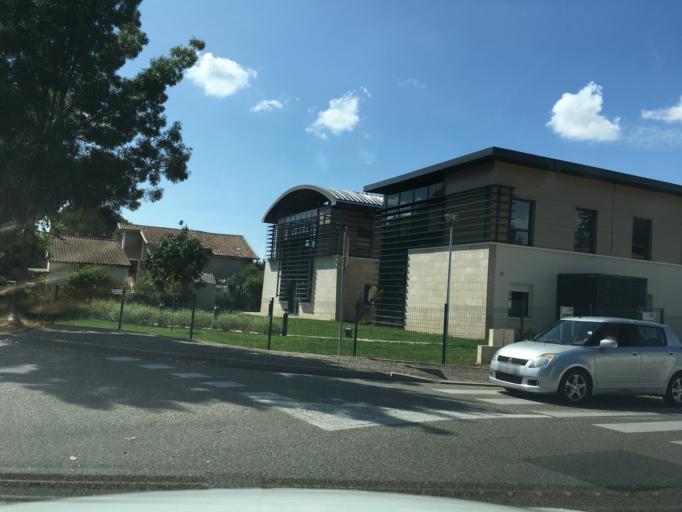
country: FR
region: Aquitaine
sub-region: Departement du Lot-et-Garonne
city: Agen
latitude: 44.1876
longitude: 0.6198
